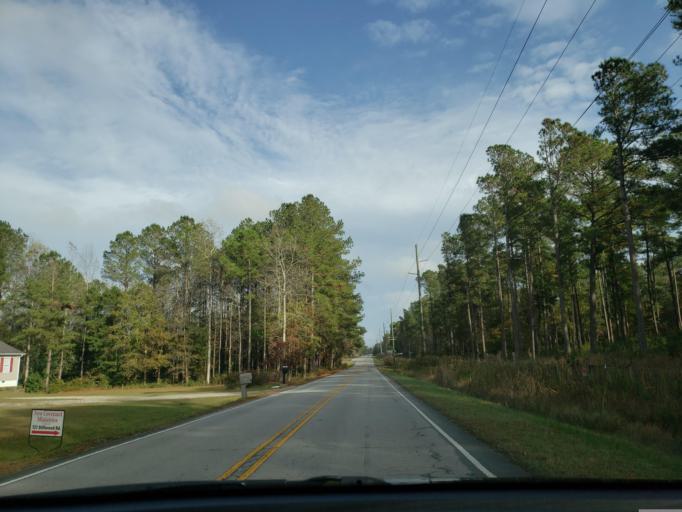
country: US
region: North Carolina
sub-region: Onslow County
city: Jacksonville
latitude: 34.6859
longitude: -77.5242
